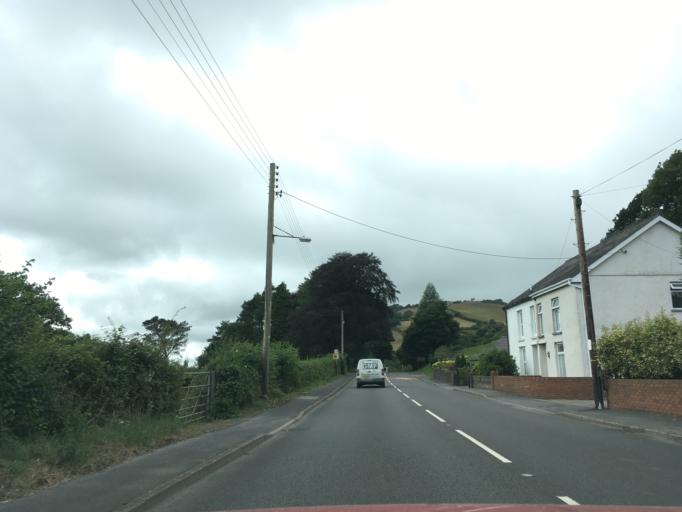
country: GB
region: Wales
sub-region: Carmarthenshire
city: Llanddarog
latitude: 51.8737
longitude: -4.1832
